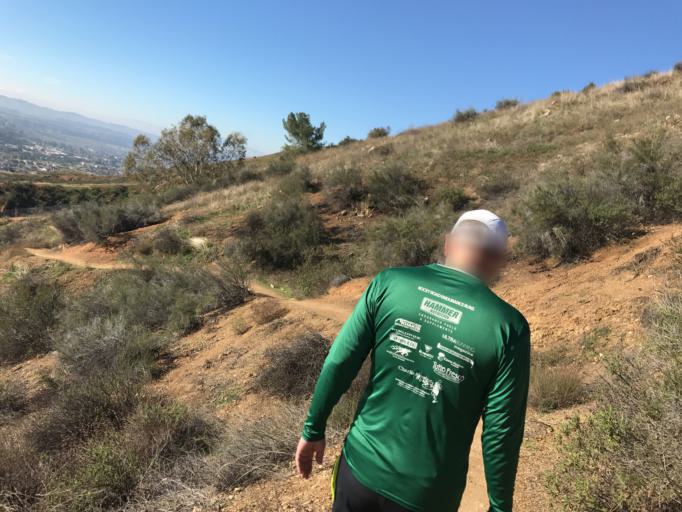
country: US
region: California
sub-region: San Bernardino County
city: Yucaipa
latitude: 34.0500
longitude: -117.0606
